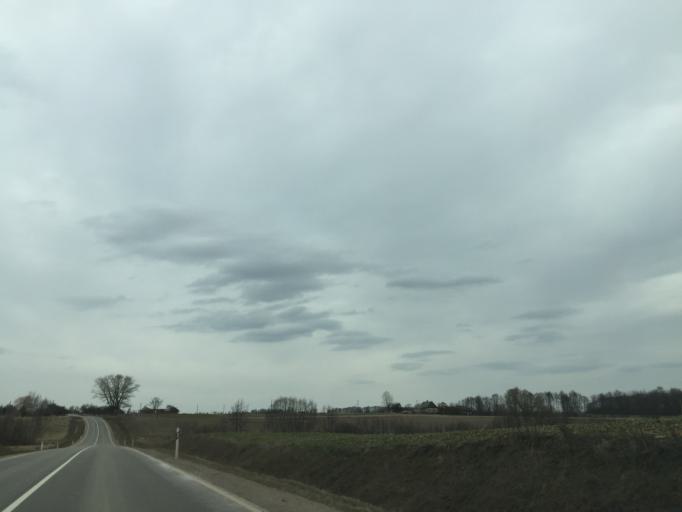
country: LV
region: Ilukste
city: Ilukste
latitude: 55.9881
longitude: 26.2901
